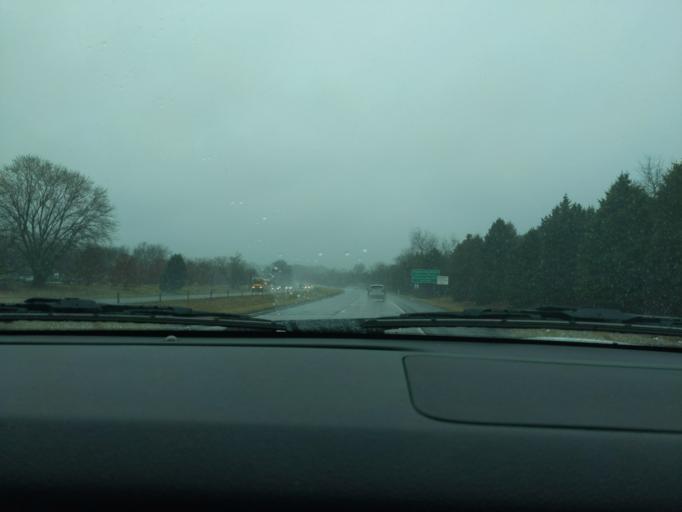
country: US
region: Pennsylvania
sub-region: Bucks County
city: Doylestown
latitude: 40.3132
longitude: -75.1481
